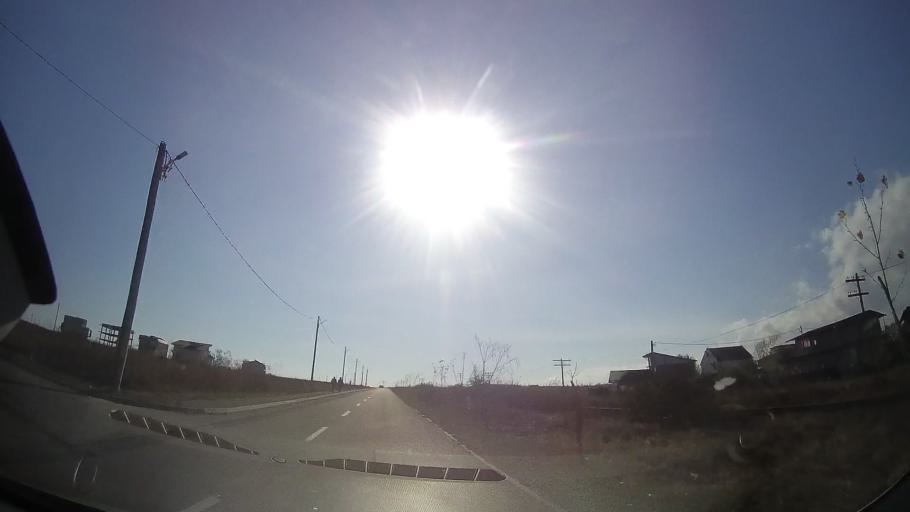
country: RO
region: Constanta
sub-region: Comuna Costinesti
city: Schitu
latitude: 43.9370
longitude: 28.6312
